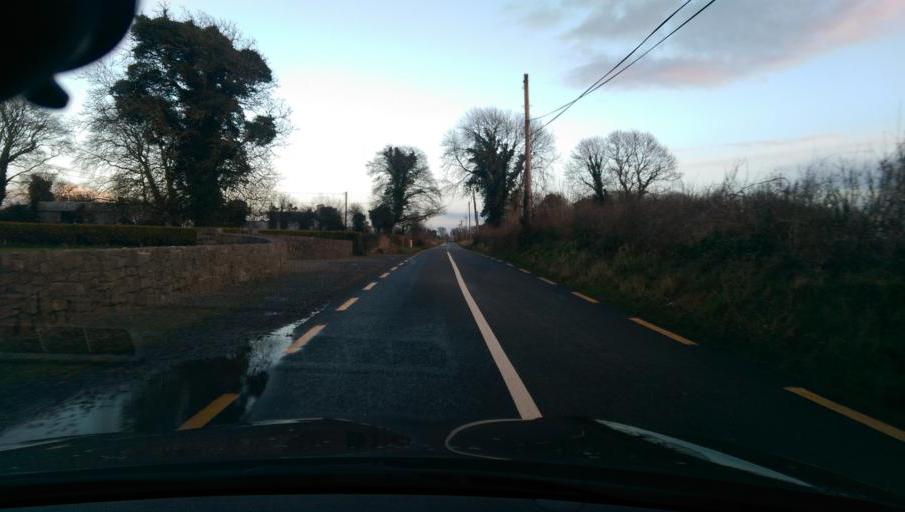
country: IE
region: Connaught
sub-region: County Galway
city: Ballinasloe
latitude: 53.3877
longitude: -8.3081
